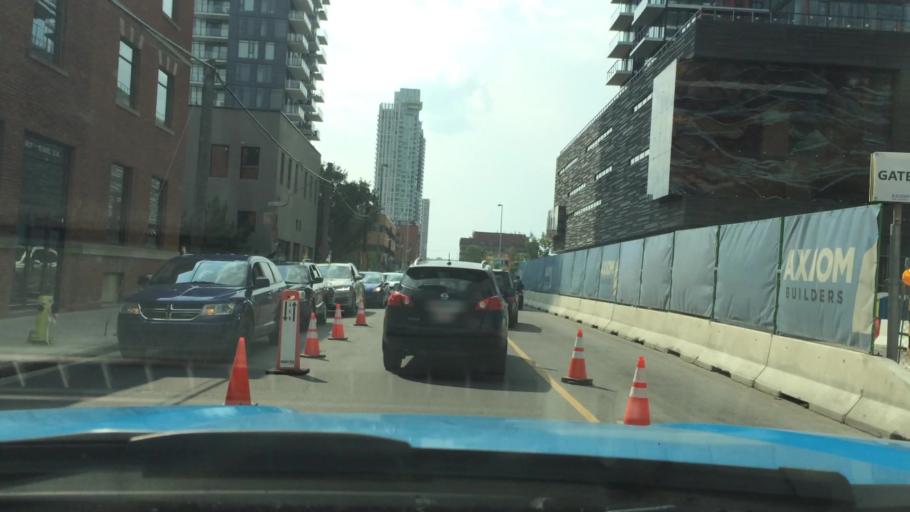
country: CA
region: Alberta
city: Calgary
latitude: 51.0436
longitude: -114.0742
